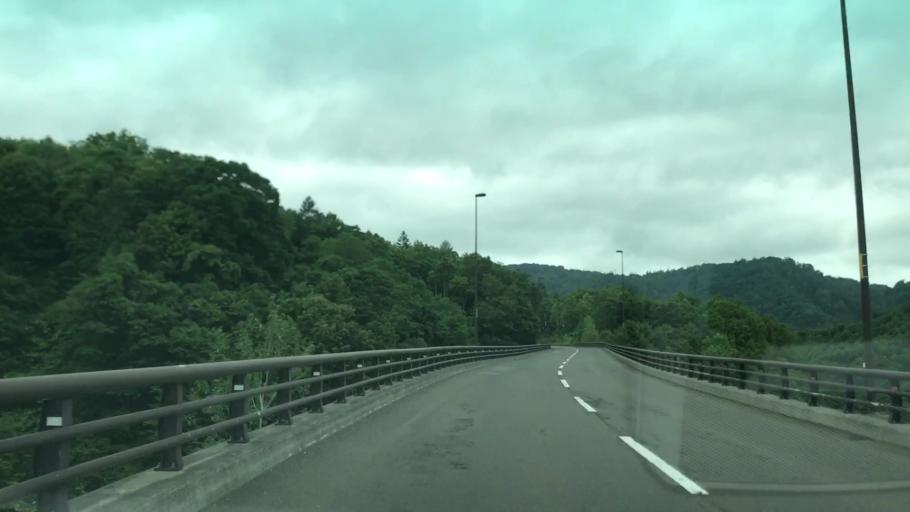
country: JP
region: Hokkaido
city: Otaru
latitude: 42.9959
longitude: 140.8786
